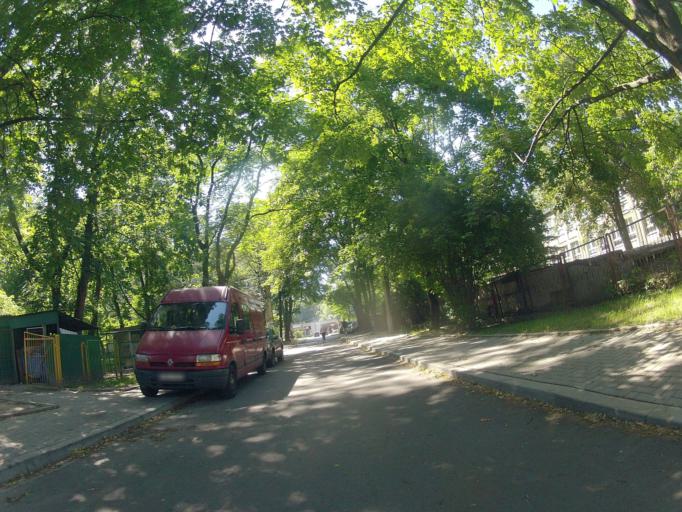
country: PL
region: Lesser Poland Voivodeship
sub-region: Powiat wielicki
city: Kokotow
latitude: 50.0735
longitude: 20.0310
